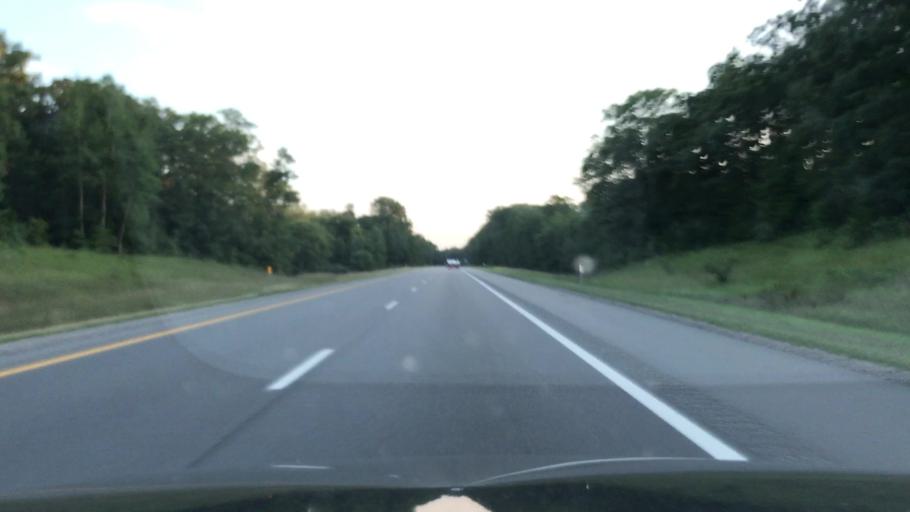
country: US
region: Michigan
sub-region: Montcalm County
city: Howard City
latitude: 43.4515
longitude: -85.4858
